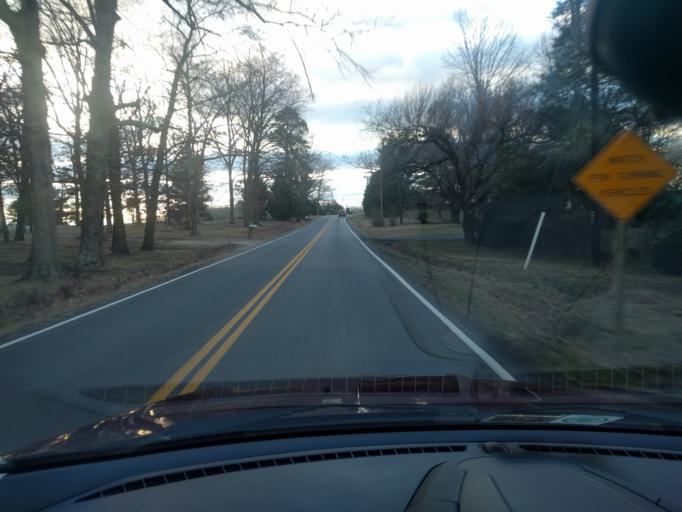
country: US
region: Virginia
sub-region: City of Bedford
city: Bedford
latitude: 37.3764
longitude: -79.5468
